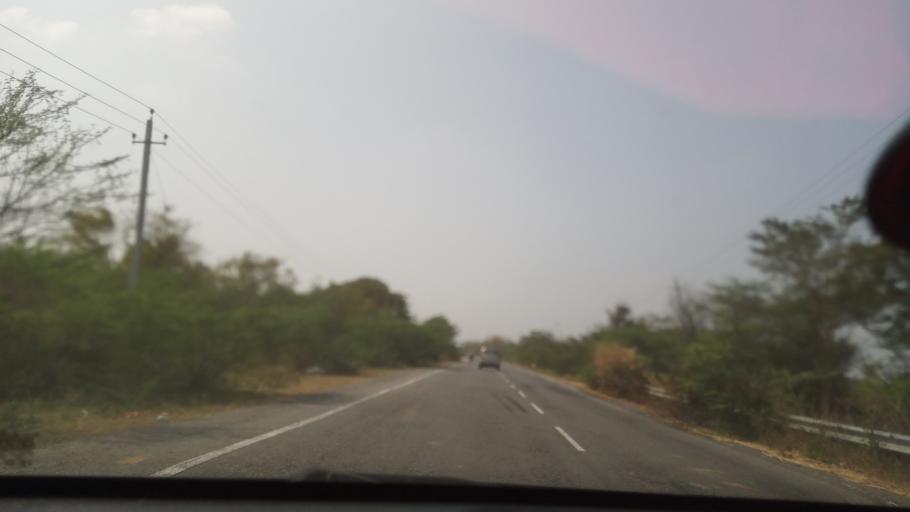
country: IN
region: Karnataka
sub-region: Mysore
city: Nanjangud
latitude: 12.0608
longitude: 76.7617
